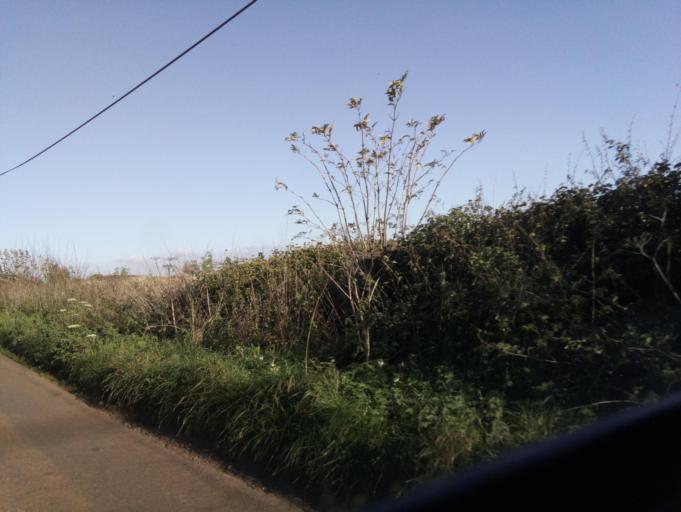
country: GB
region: England
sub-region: Dorset
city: Sherborne
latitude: 51.0065
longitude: -2.5104
